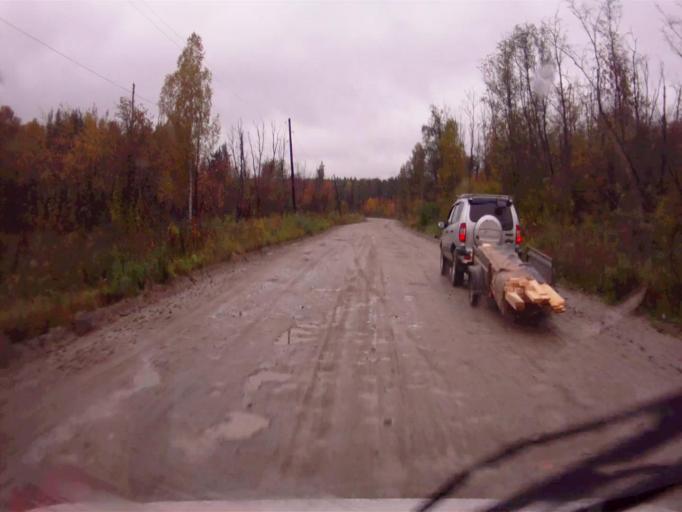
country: RU
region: Chelyabinsk
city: Kyshtym
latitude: 55.7385
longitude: 60.5119
